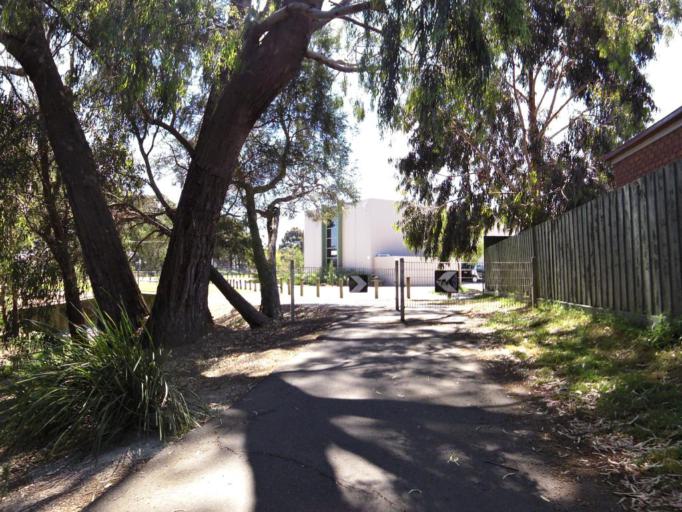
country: AU
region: Victoria
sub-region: Knox
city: Ferntree Gully
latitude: -37.8931
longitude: 145.3014
